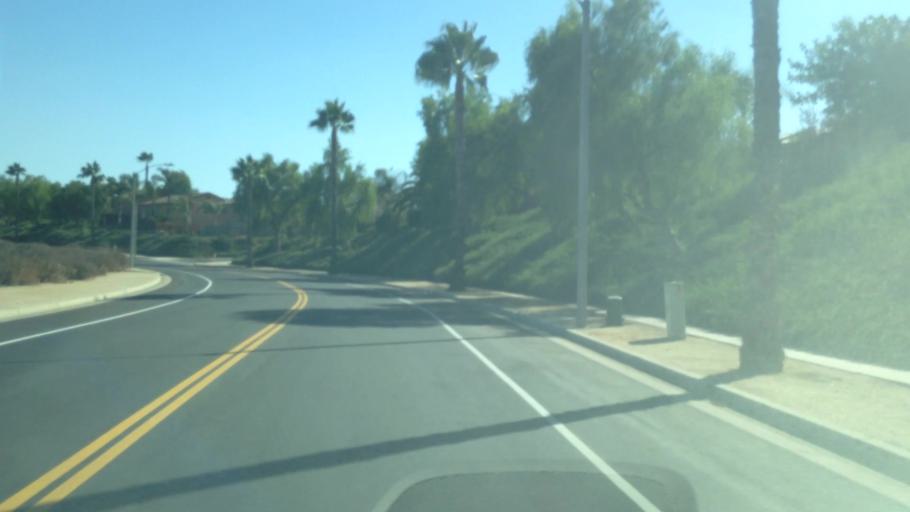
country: US
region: California
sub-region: Riverside County
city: Home Gardens
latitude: 33.8693
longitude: -117.4447
